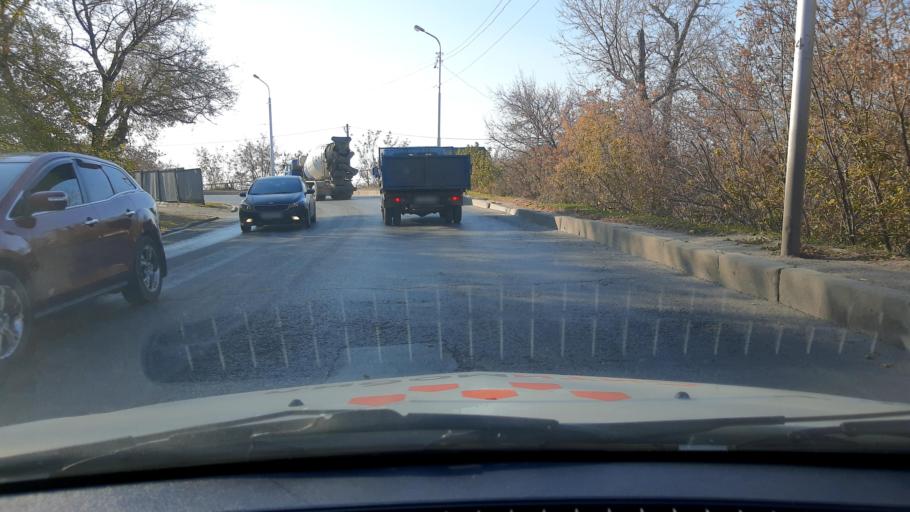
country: RU
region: Bashkortostan
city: Ufa
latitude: 54.7414
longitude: 55.9340
